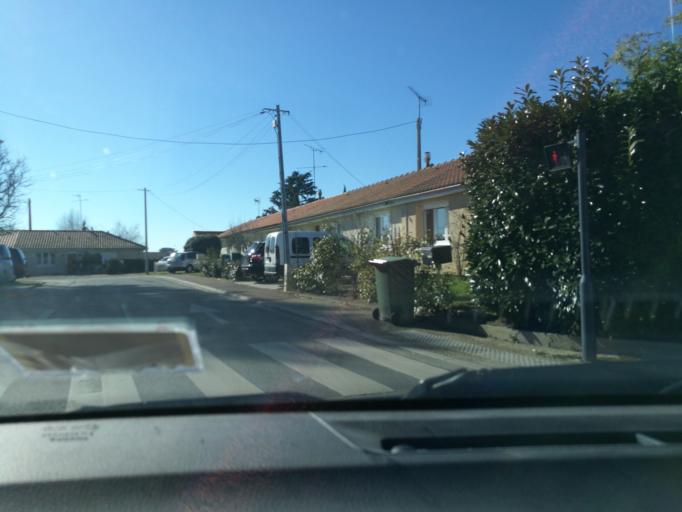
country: FR
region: Centre
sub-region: Departement du Loiret
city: Saint-Jean-de-la-Ruelle
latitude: 47.9018
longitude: 1.8652
